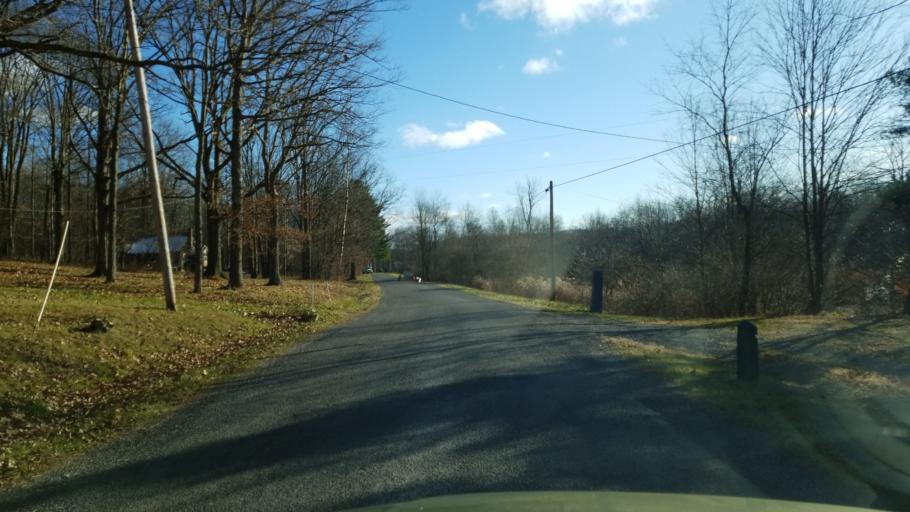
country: US
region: Pennsylvania
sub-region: Jefferson County
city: Brockway
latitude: 41.2643
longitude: -78.8043
